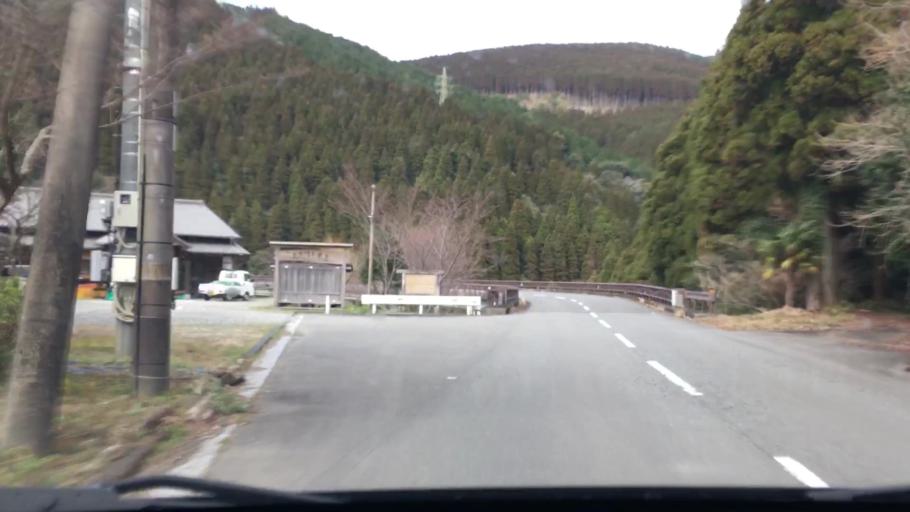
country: JP
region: Miyazaki
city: Nichinan
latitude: 31.6618
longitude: 131.3247
